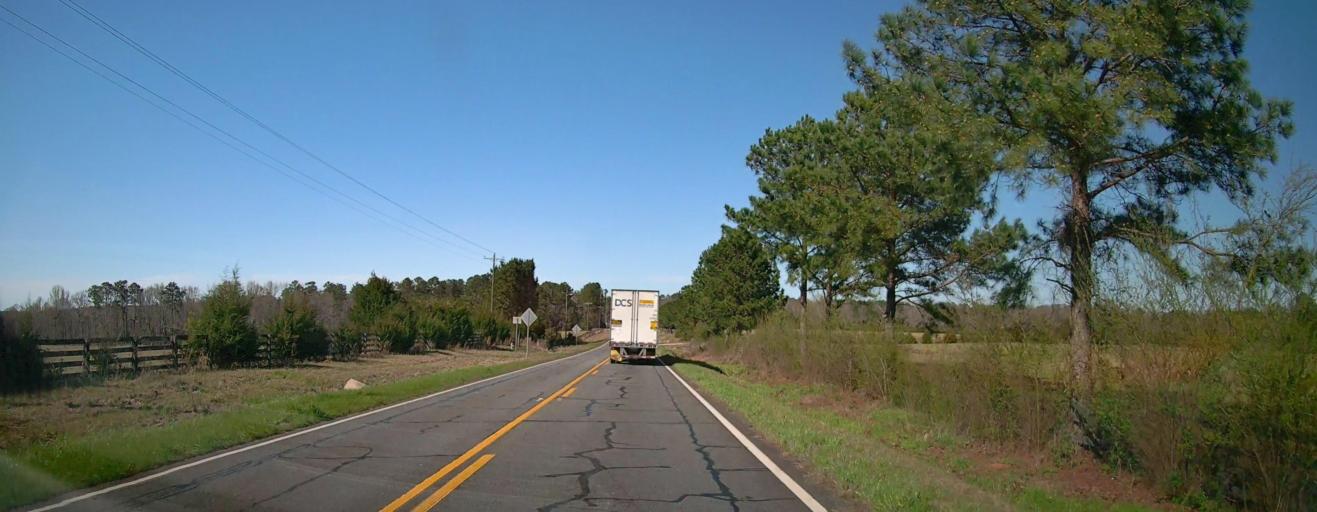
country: US
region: Georgia
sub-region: Butts County
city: Indian Springs
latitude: 33.1821
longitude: -83.9589
